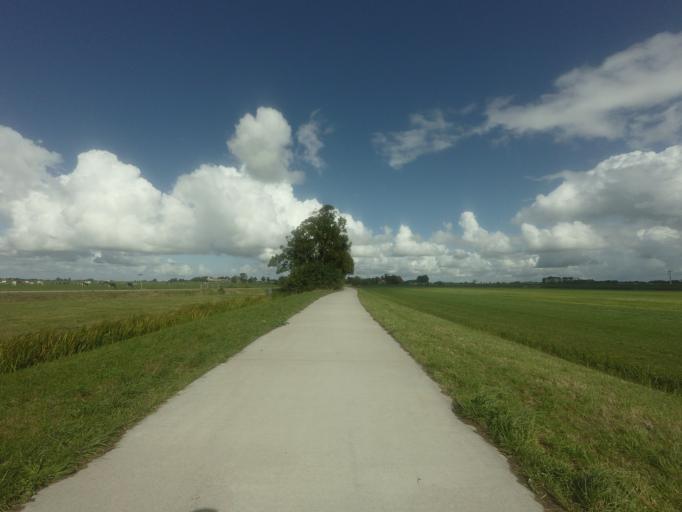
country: NL
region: Friesland
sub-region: Gemeente Littenseradiel
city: Makkum
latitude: 53.0904
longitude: 5.7044
